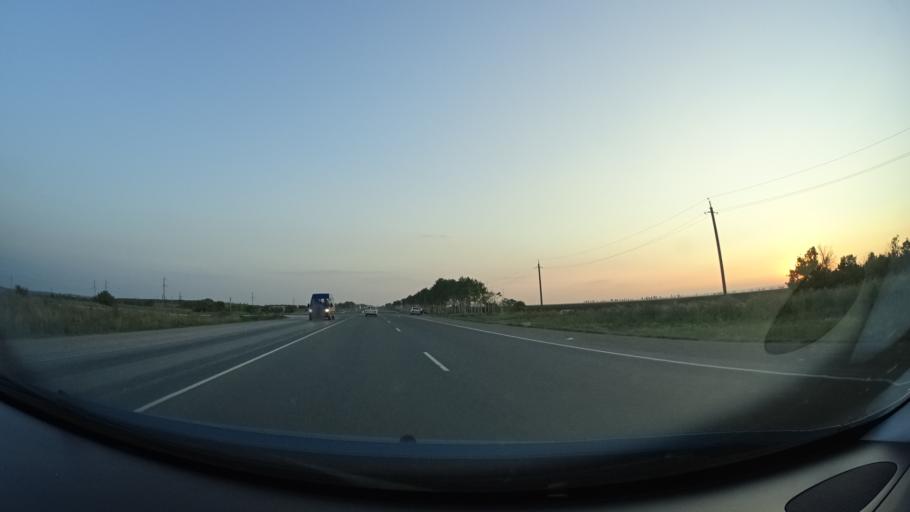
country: RU
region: Samara
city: Sukhodol
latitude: 53.8605
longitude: 51.1733
